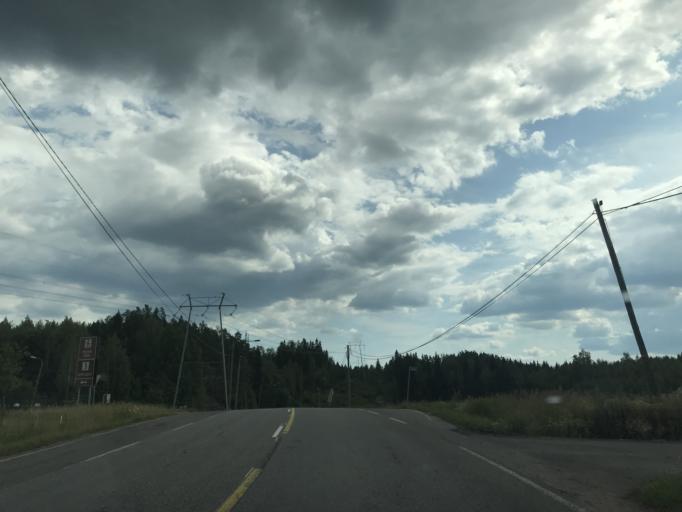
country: FI
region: Uusimaa
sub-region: Helsinki
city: Vihti
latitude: 60.3789
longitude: 24.3566
